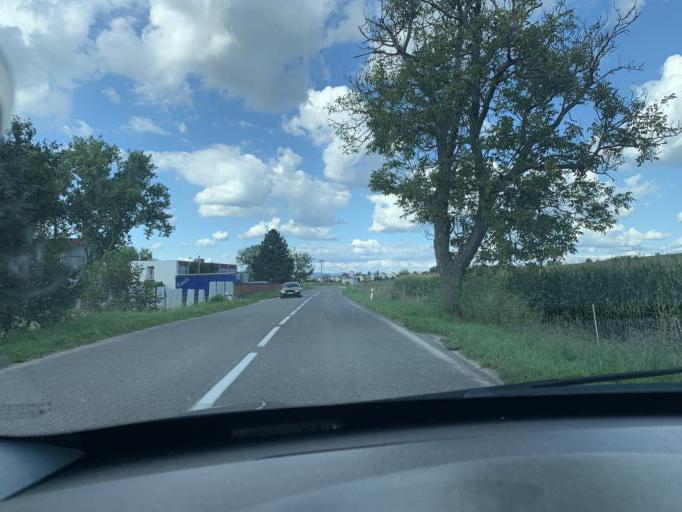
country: SK
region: Trenciansky
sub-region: Okres Trencin
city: Trencin
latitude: 48.8326
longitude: 17.9767
